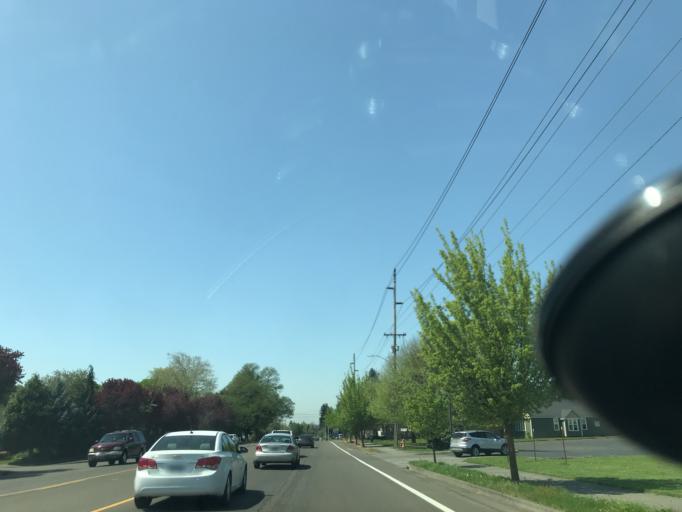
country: US
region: Oregon
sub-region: Multnomah County
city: Gresham
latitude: 45.4917
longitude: -122.4813
